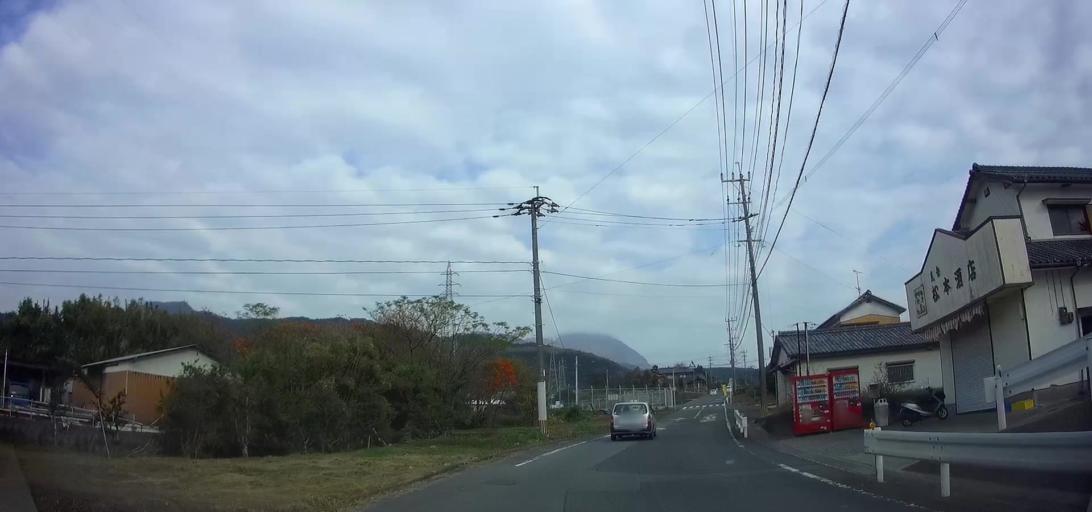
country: JP
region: Nagasaki
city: Shimabara
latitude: 32.6895
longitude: 130.2953
